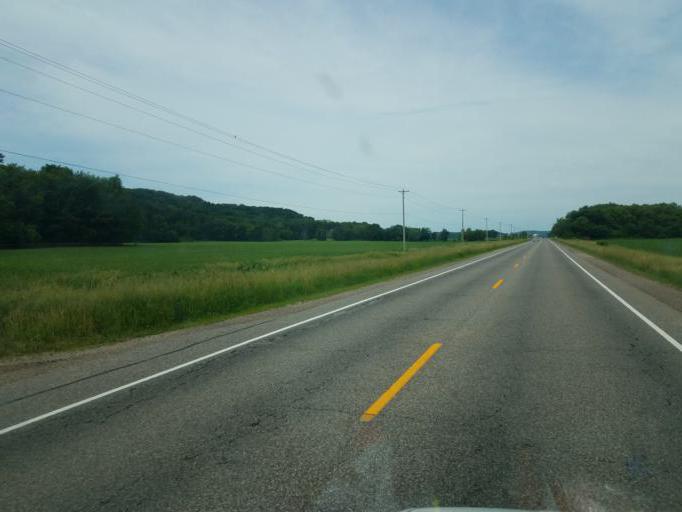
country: US
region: Wisconsin
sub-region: Juneau County
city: Mauston
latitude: 43.7890
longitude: -90.1161
